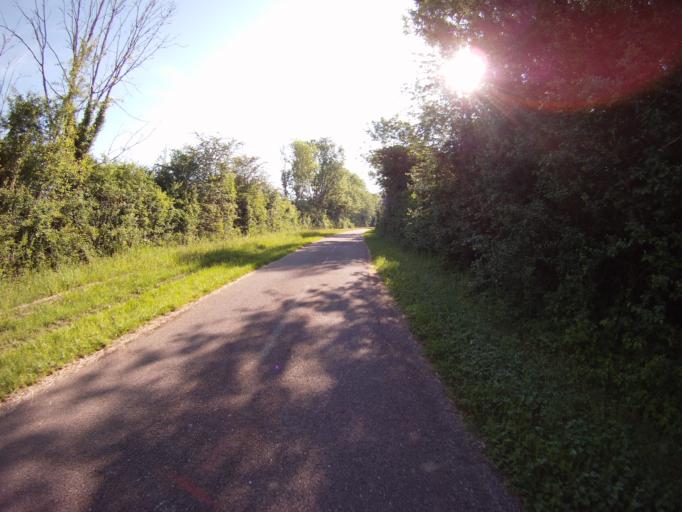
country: FR
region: Lorraine
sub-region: Departement de Meurthe-et-Moselle
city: Lay-Saint-Christophe
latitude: 48.7458
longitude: 6.1925
